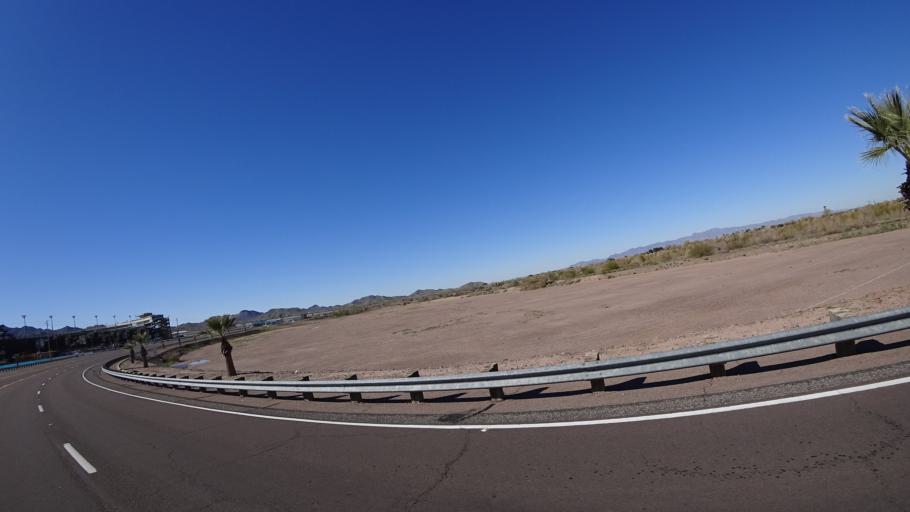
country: US
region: Arizona
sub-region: Maricopa County
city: Avondale
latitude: 33.3789
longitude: -112.3096
